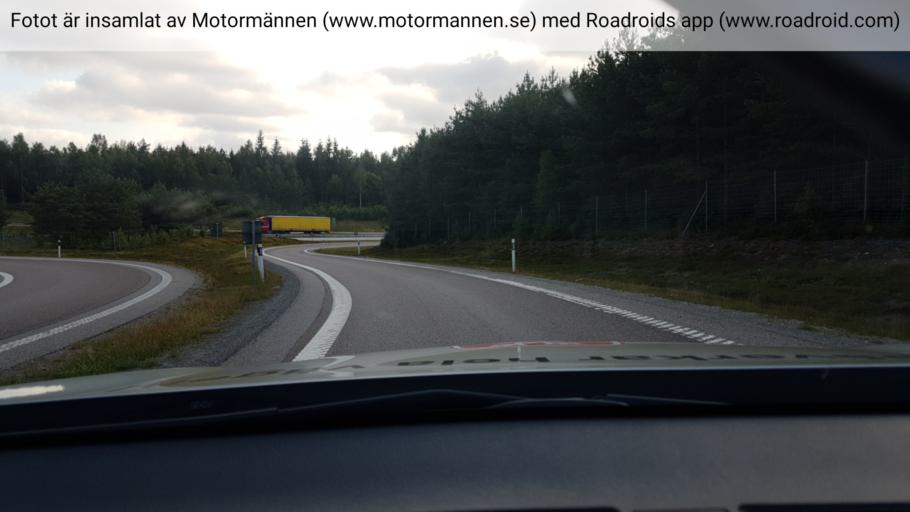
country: SE
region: Vaestra Goetaland
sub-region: Harryda Kommun
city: Ravlanda
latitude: 57.6737
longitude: 12.4919
